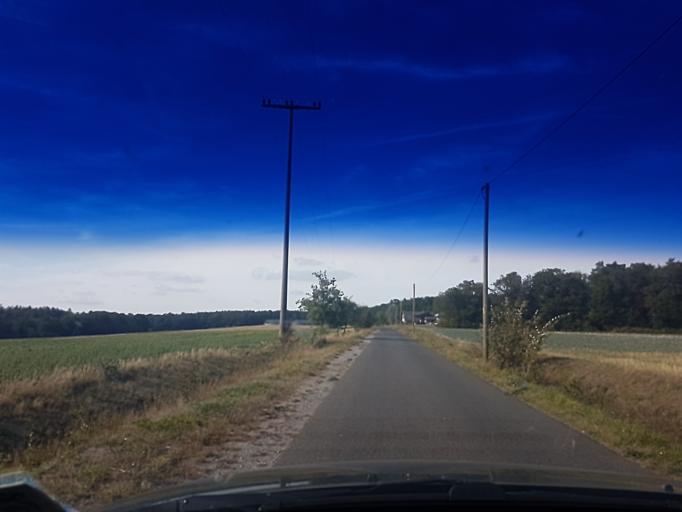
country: DE
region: Bavaria
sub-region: Upper Franconia
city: Burgwindheim
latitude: 49.7815
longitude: 10.5422
